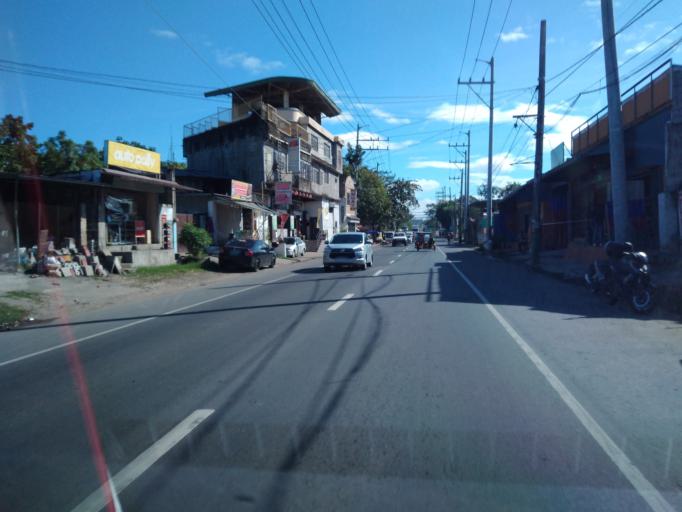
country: PH
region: Central Luzon
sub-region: Province of Bulacan
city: Santa Maria
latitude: 14.8301
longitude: 120.9624
